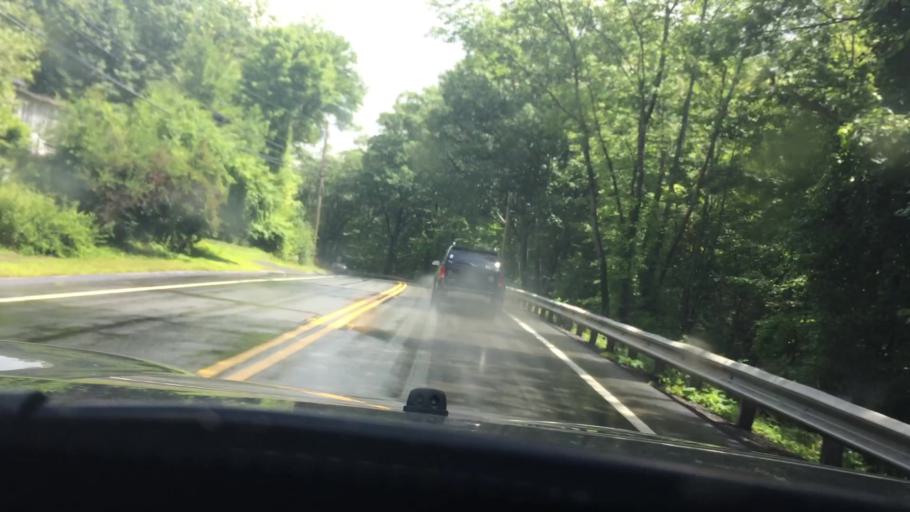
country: US
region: Massachusetts
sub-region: Worcester County
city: Phillipston
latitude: 42.5699
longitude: -72.1526
